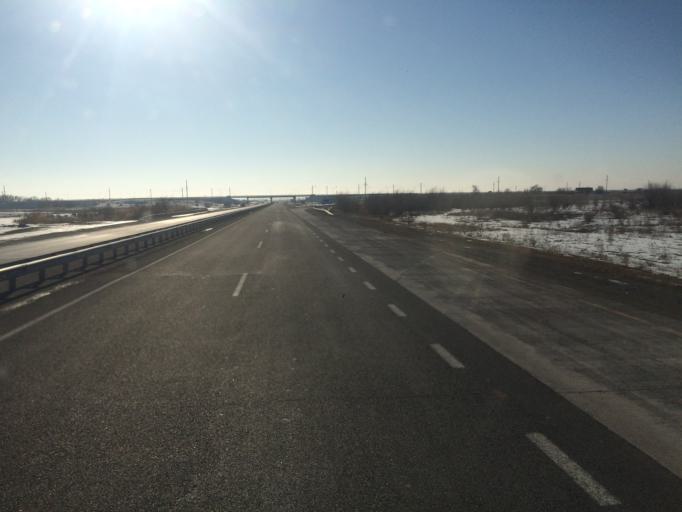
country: KG
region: Chuy
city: Sokuluk
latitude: 43.2802
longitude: 74.2346
